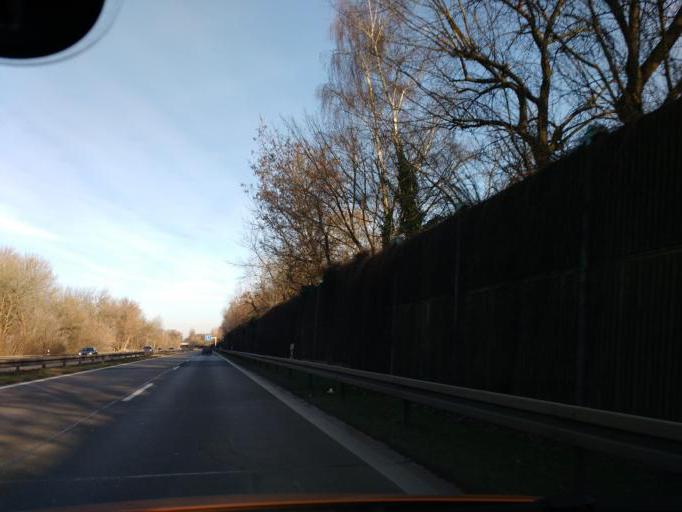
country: DE
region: Berlin
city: Blankenburg
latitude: 52.6008
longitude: 13.4471
